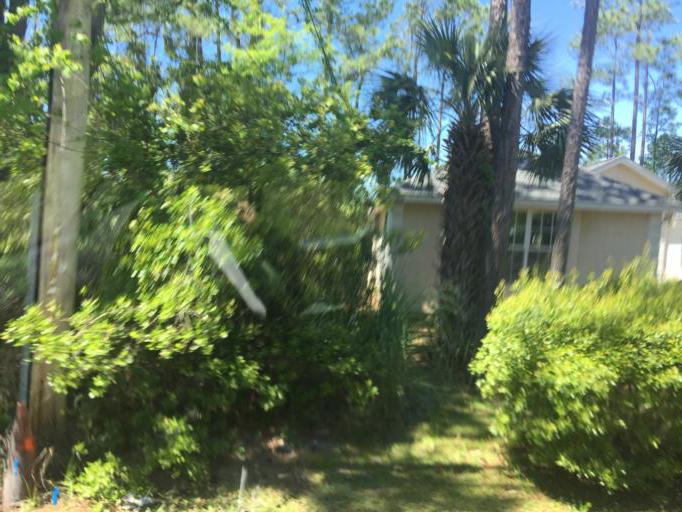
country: US
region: Florida
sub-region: Bay County
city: Laguna Beach
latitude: 30.2632
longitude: -85.9702
